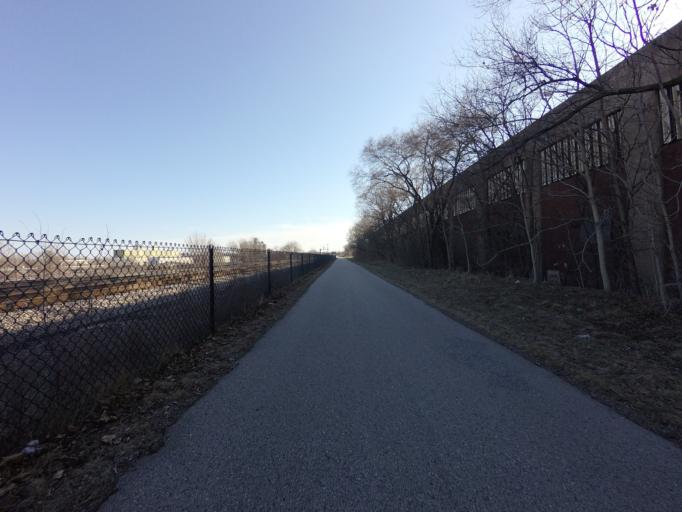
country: US
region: Wisconsin
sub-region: Milwaukee County
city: Milwaukee
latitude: 43.0141
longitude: -87.9089
